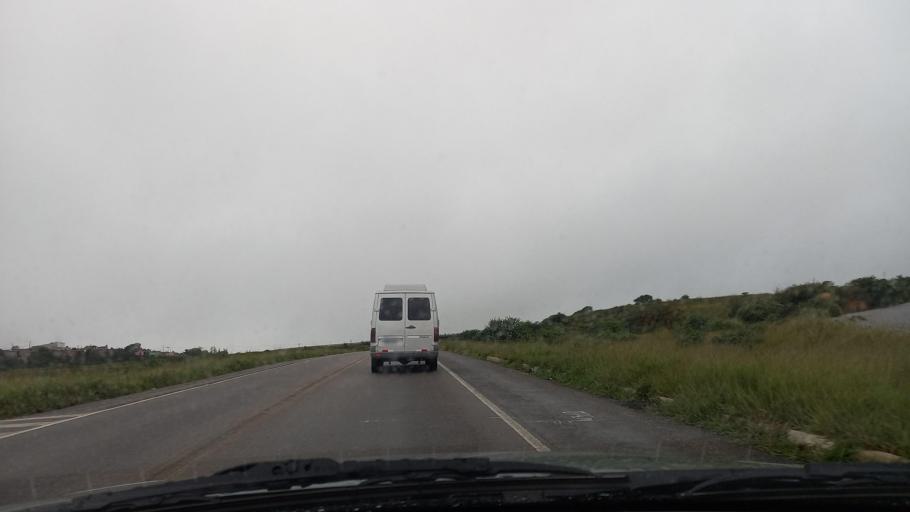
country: BR
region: Pernambuco
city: Garanhuns
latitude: -8.8738
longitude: -36.5077
